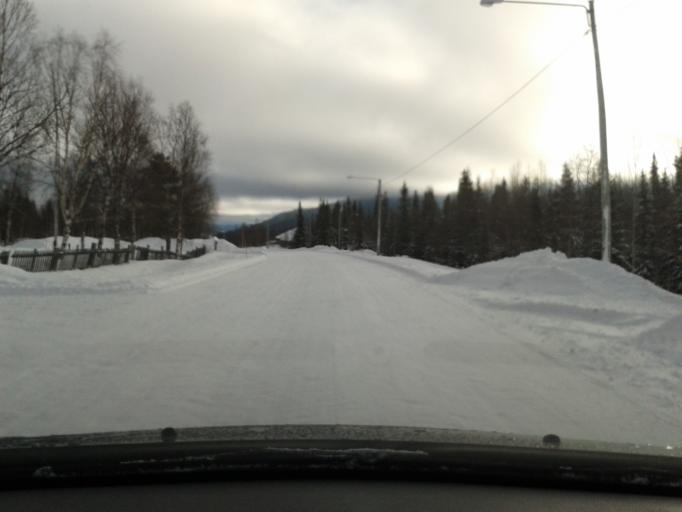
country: SE
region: Vaesterbotten
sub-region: Vilhelmina Kommun
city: Sjoberg
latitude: 65.2534
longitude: 15.5334
